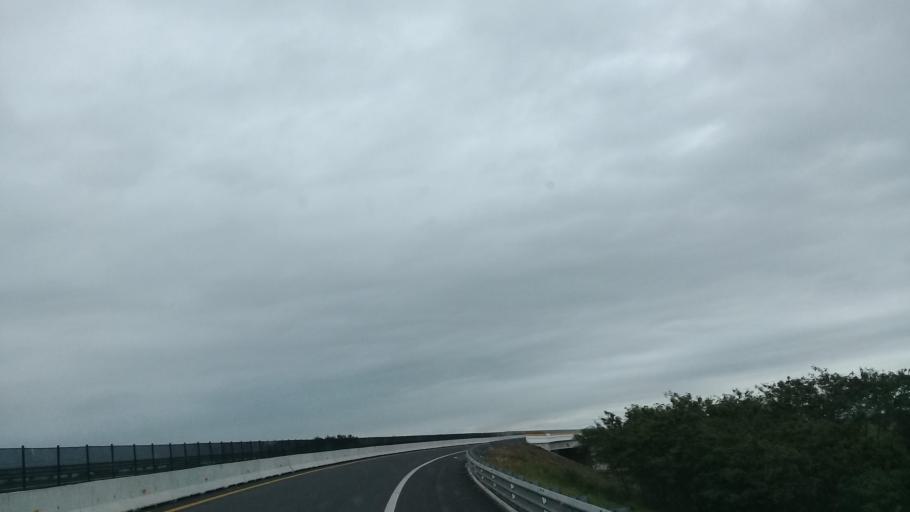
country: MX
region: Veracruz
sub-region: La Antigua
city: Nicolas Blanco (San Pancho)
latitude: 19.3586
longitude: -96.3483
